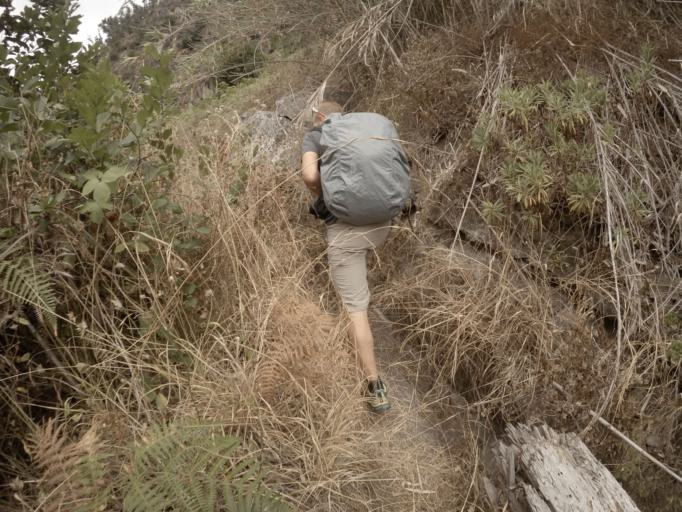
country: PT
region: Madeira
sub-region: Camara de Lobos
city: Curral das Freiras
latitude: 32.6824
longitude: -16.9594
